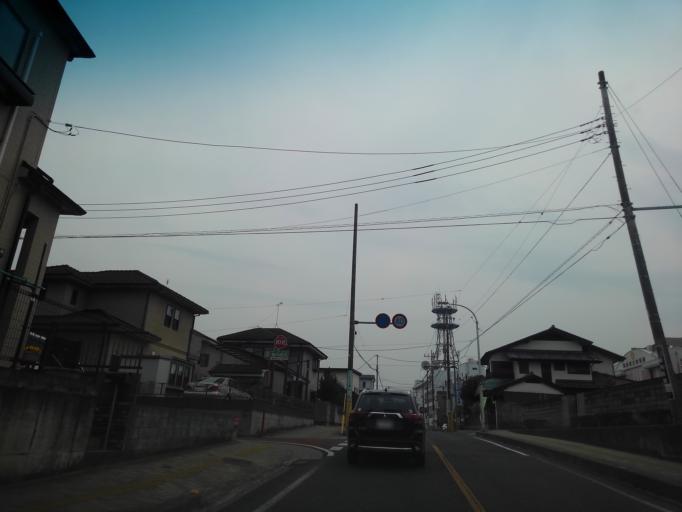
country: JP
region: Saitama
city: Tokorozawa
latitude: 35.7904
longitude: 139.4639
